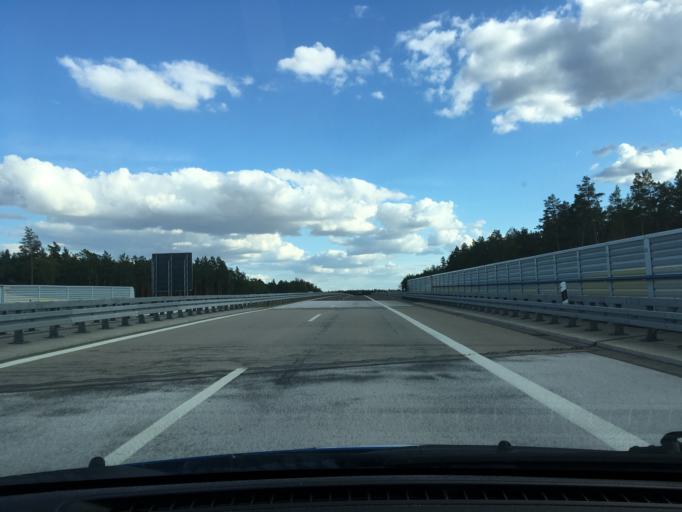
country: DE
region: Mecklenburg-Vorpommern
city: Ludwigslust
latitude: 53.3395
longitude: 11.5220
